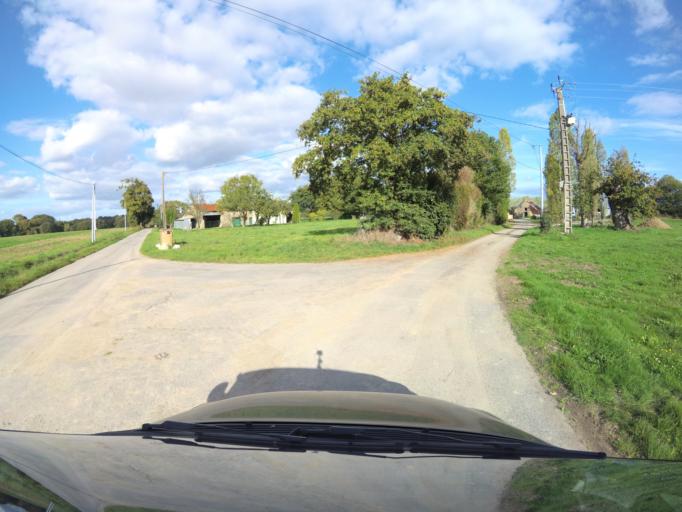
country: FR
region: Brittany
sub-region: Departement du Morbihan
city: Saint-Martin-sur-Oust
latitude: 47.7353
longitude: -2.2418
